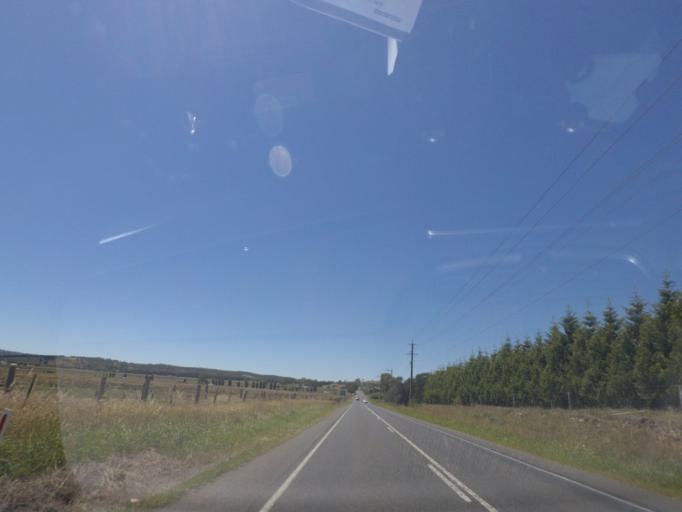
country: AU
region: Victoria
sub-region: Whittlesea
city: Whittlesea
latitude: -37.4241
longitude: 145.0221
